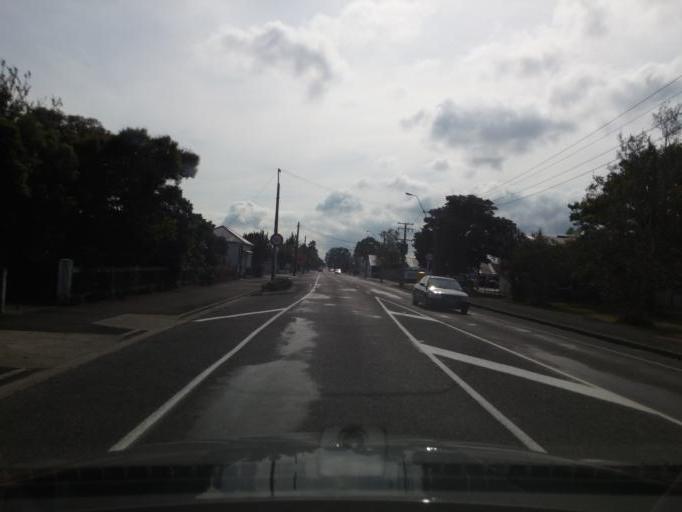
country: NZ
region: Wellington
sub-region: Masterton District
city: Masterton
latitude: -41.0887
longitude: 175.4511
